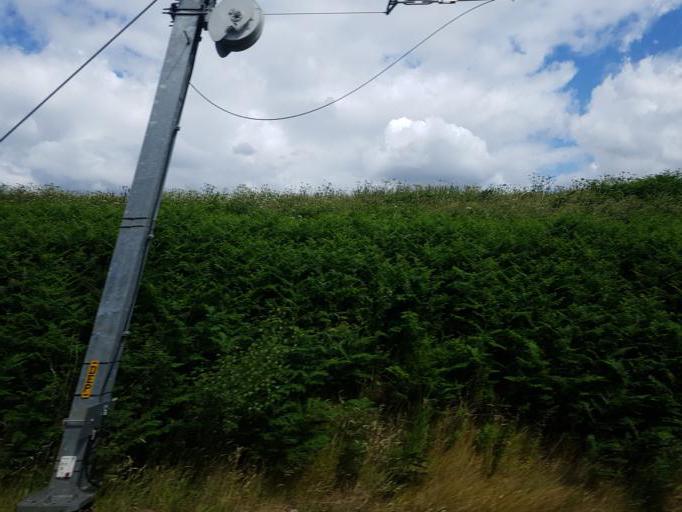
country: GB
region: Scotland
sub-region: Falkirk
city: Polmont
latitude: 55.9794
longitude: -3.6727
